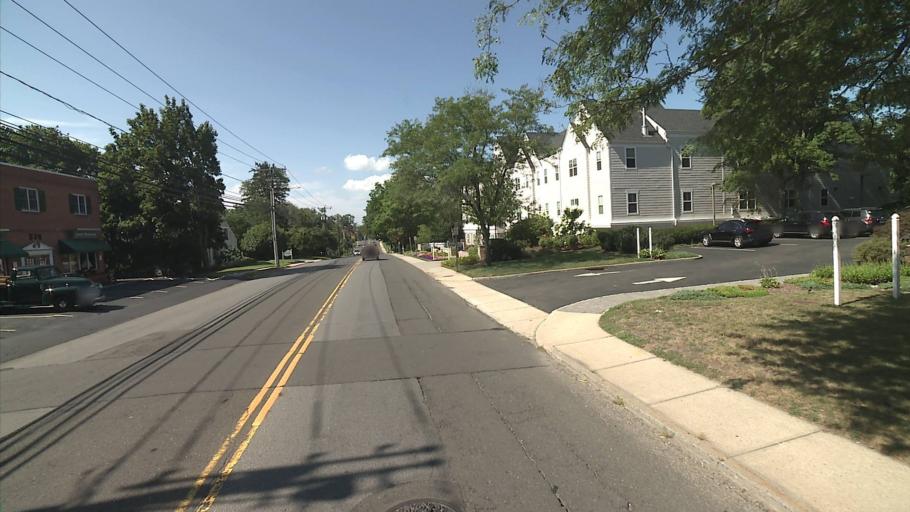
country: US
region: Connecticut
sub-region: Fairfield County
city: Darien
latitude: 41.0828
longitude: -73.4645
